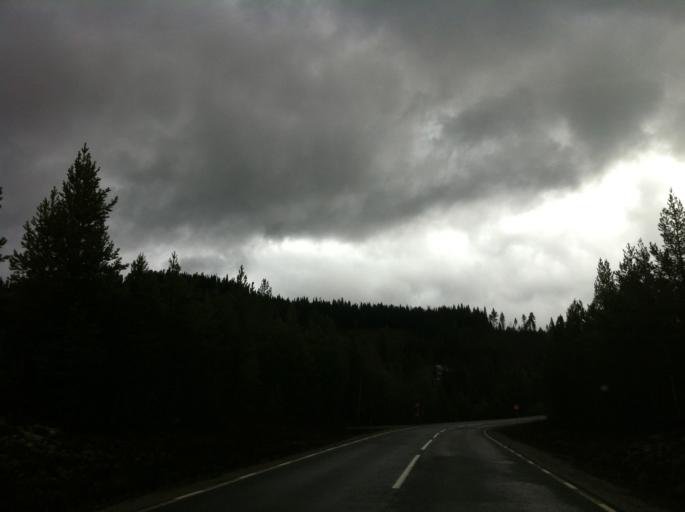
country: NO
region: Hedmark
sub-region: Engerdal
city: Engerdal
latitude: 62.4254
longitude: 12.7304
